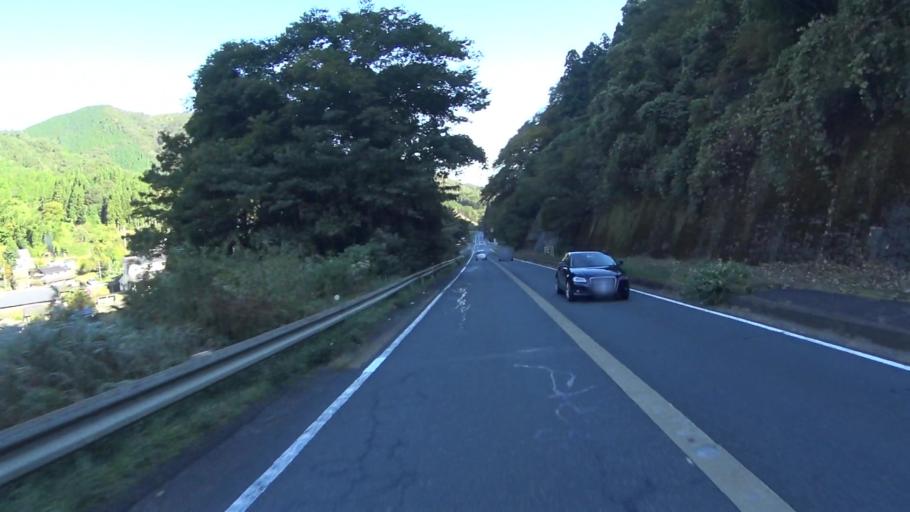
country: JP
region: Kyoto
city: Fukuchiyama
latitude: 35.3970
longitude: 135.0873
